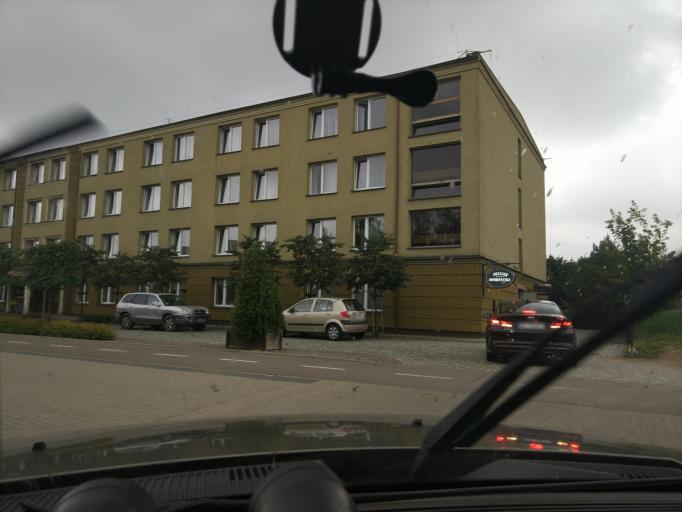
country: PL
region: Podlasie
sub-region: Bialystok
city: Bialystok
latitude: 53.1442
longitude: 23.1922
